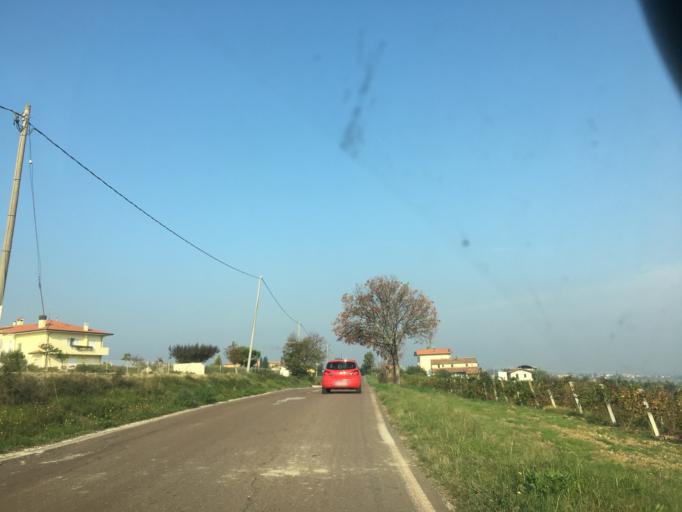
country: IT
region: Emilia-Romagna
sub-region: Provincia di Rimini
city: San Clemente
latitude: 43.9475
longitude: 12.6156
